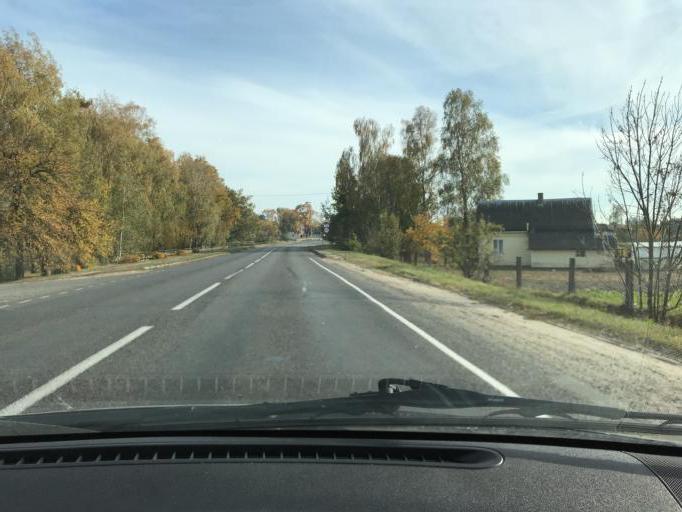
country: BY
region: Brest
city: Asnyezhytsy
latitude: 52.1990
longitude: 26.0655
